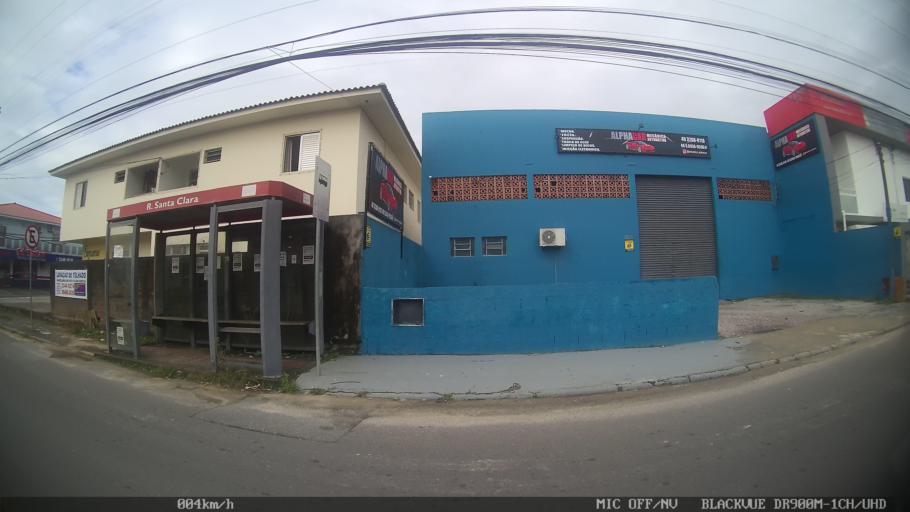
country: BR
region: Santa Catarina
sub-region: Sao Jose
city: Campinas
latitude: -27.5581
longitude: -48.6227
